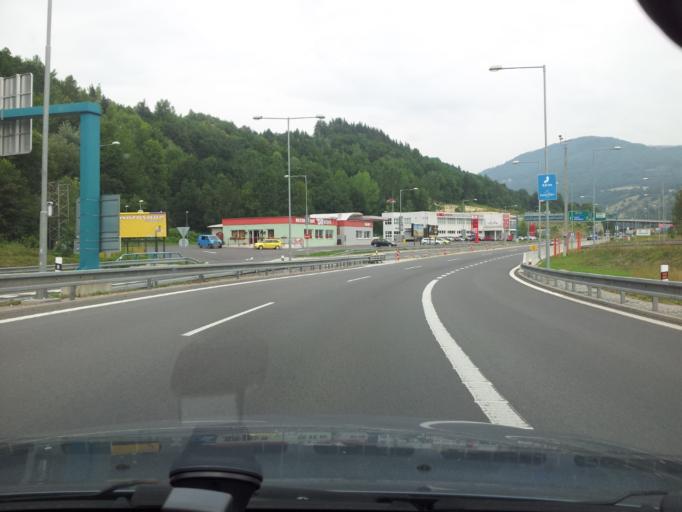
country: SK
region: Banskobystricky
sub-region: Okres Banska Bystrica
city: Banska Bystrica
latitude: 48.7514
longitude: 19.1390
